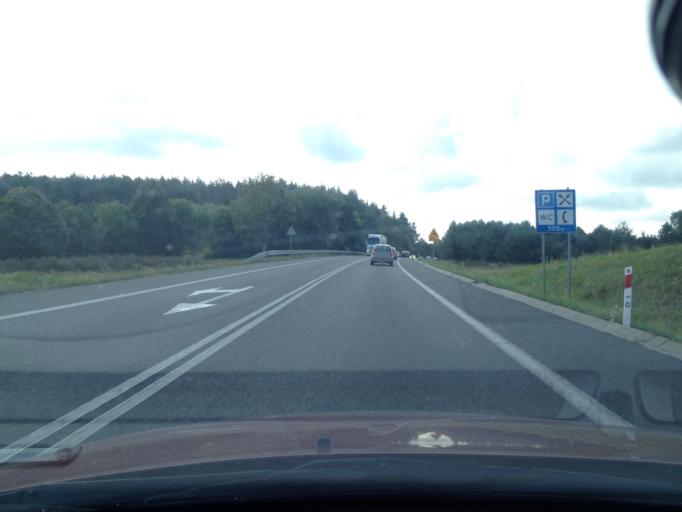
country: PL
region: West Pomeranian Voivodeship
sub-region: Powiat goleniowski
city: Przybiernow
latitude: 53.7459
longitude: 14.7751
